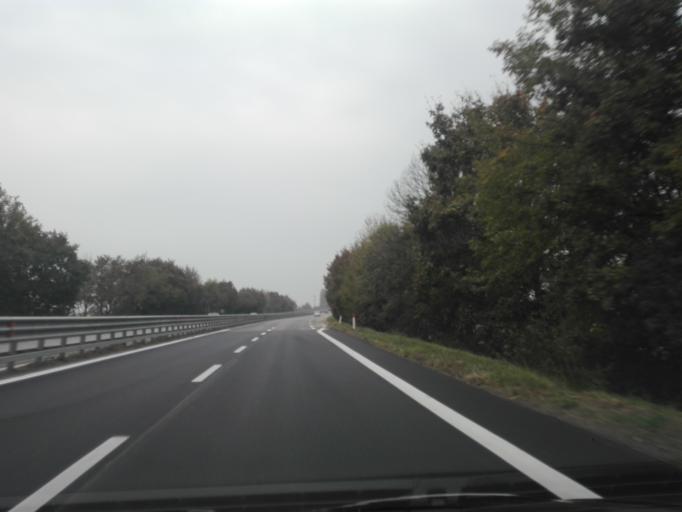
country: IT
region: Veneto
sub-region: Provincia di Verona
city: Villa Bartolomea
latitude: 45.1624
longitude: 11.3067
